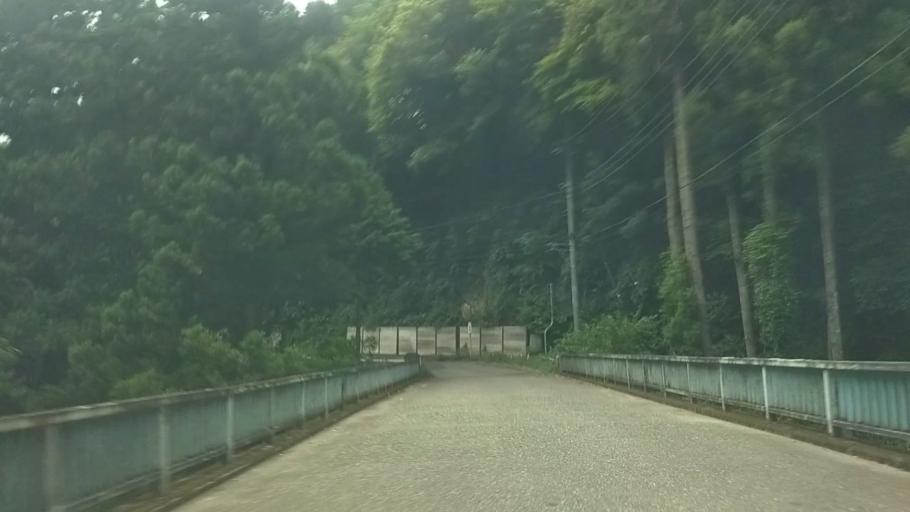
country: JP
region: Chiba
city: Kawaguchi
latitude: 35.1897
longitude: 140.1405
